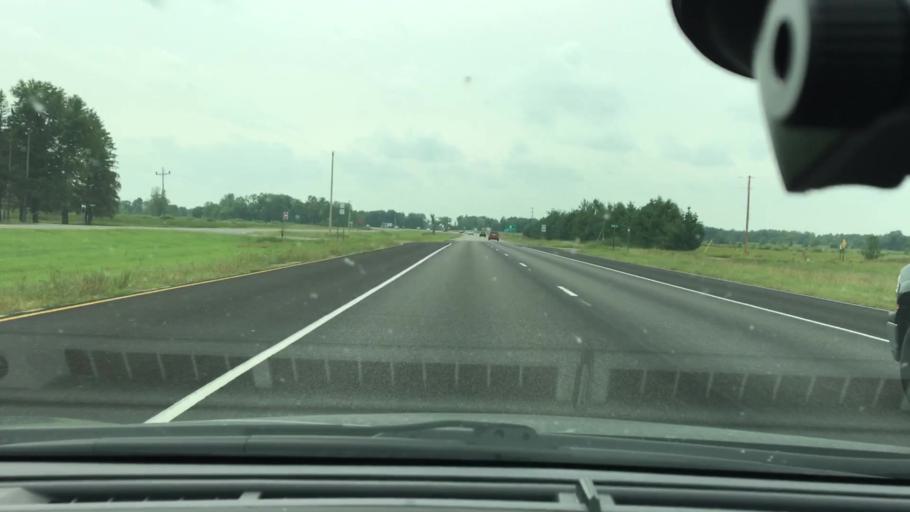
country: US
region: Minnesota
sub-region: Mille Lacs County
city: Milaca
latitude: 45.7941
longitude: -93.6542
